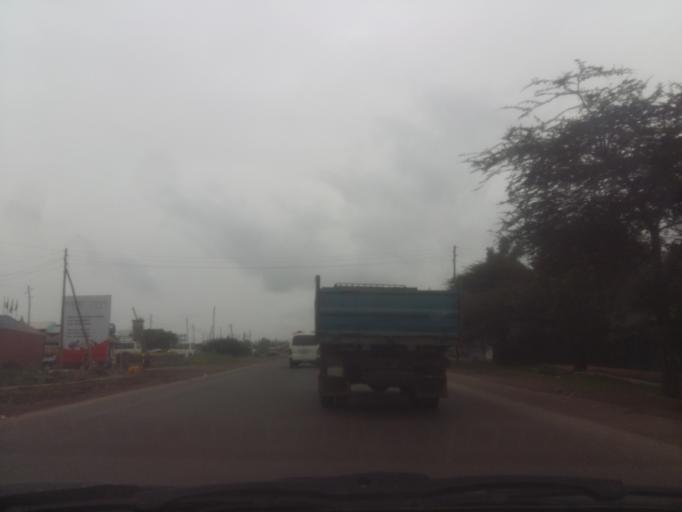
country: ET
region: Oromiya
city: Bishoftu
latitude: 8.8159
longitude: 38.8828
